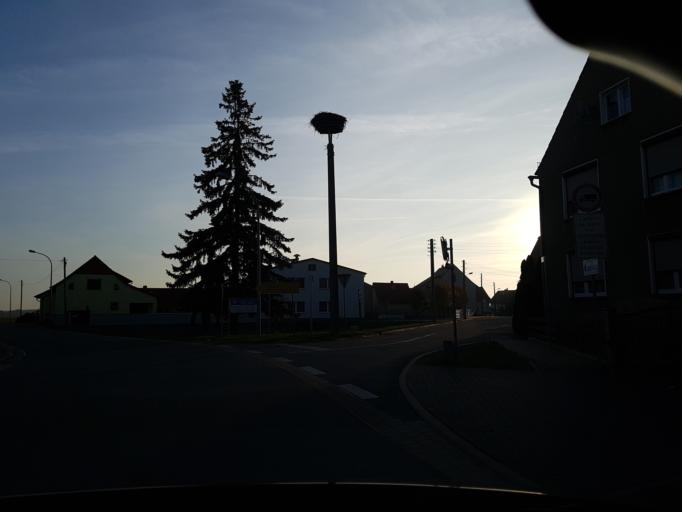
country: DE
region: Saxony
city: Nauwalde
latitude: 51.4581
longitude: 13.4262
